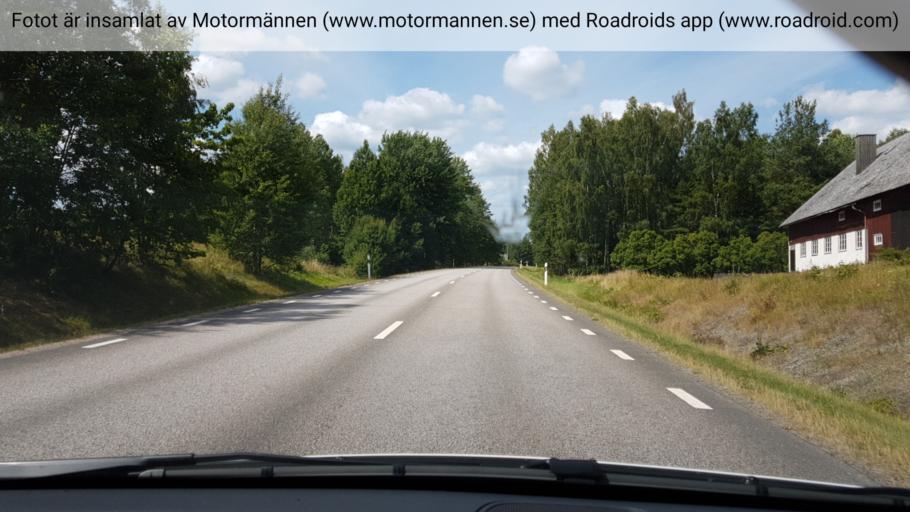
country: SE
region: Vaestra Goetaland
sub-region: Mariestads Kommun
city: Mariestad
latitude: 58.6671
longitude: 13.8641
